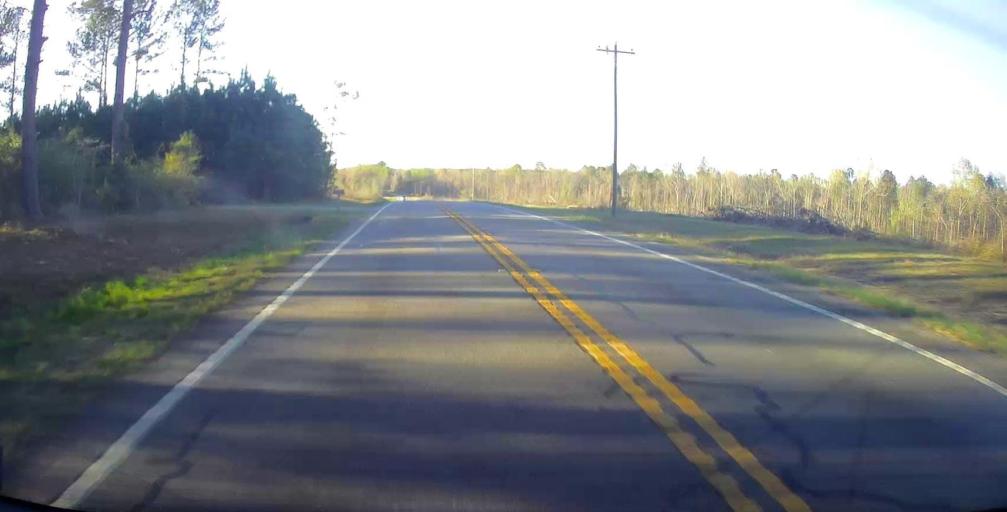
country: US
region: Georgia
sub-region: Wilcox County
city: Abbeville
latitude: 32.0461
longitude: -83.2605
